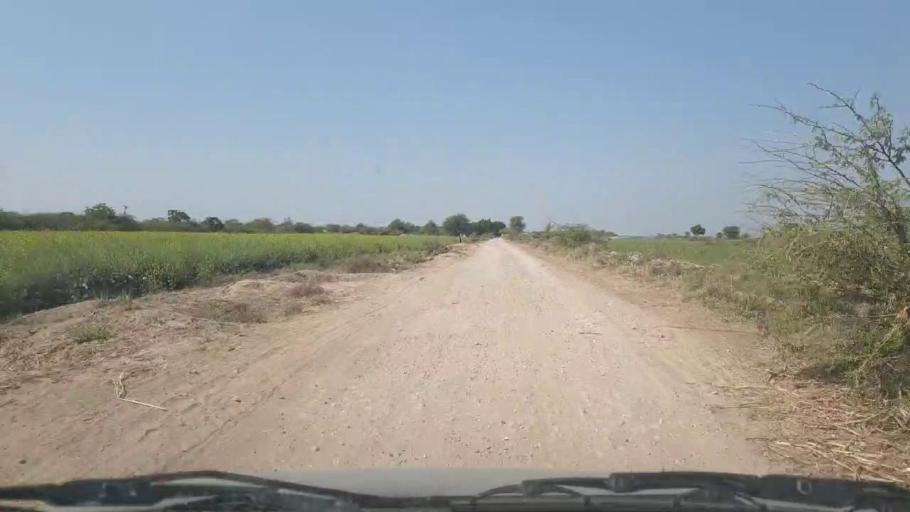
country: PK
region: Sindh
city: Samaro
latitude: 25.2252
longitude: 69.3261
